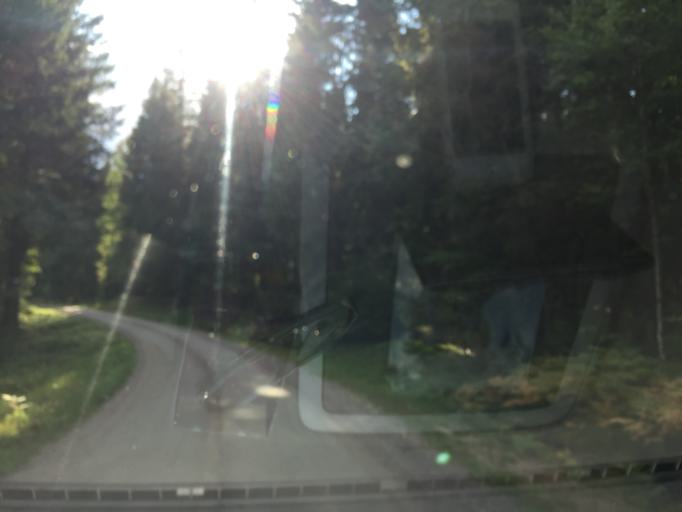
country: SE
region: Soedermanland
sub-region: Vingakers Kommun
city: Vingaker
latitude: 59.0019
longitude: 15.7430
